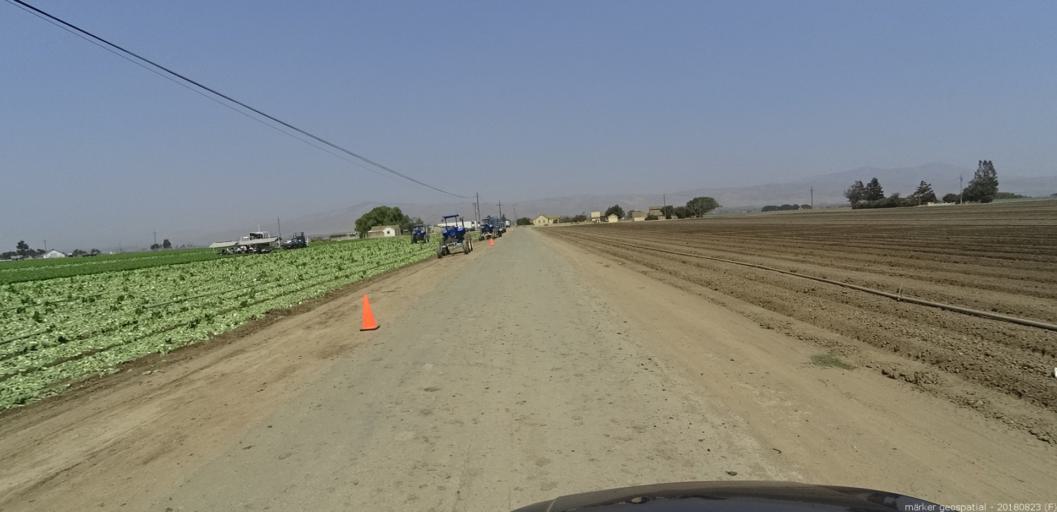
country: US
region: California
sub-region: Monterey County
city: Soledad
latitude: 36.3990
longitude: -121.3423
